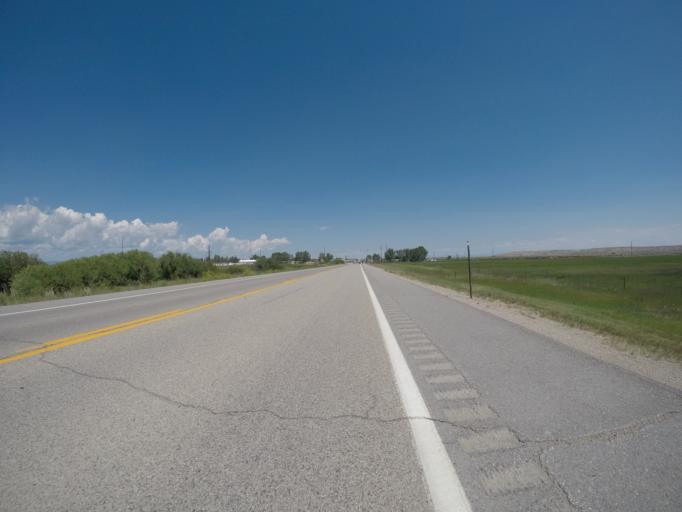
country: US
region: Wyoming
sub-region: Sublette County
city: Marbleton
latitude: 42.5327
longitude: -110.1098
